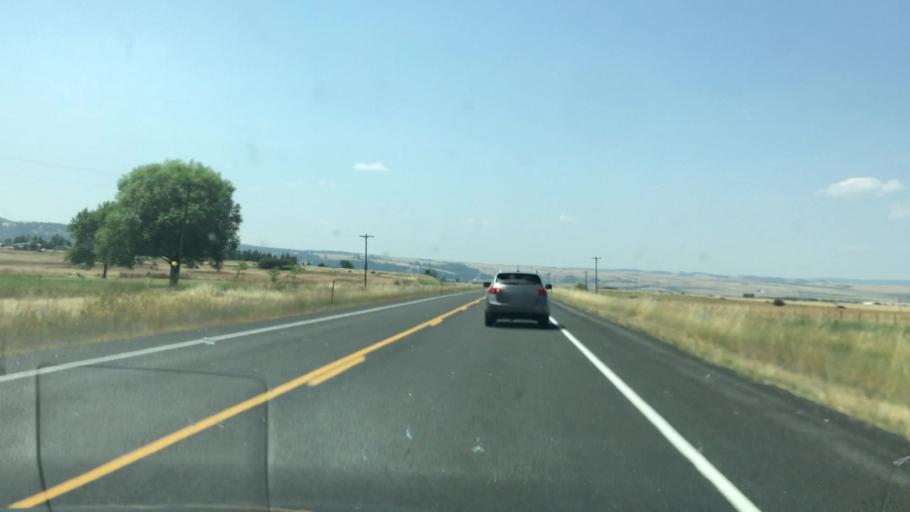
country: US
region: Idaho
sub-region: Idaho County
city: Grangeville
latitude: 45.9116
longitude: -116.1638
